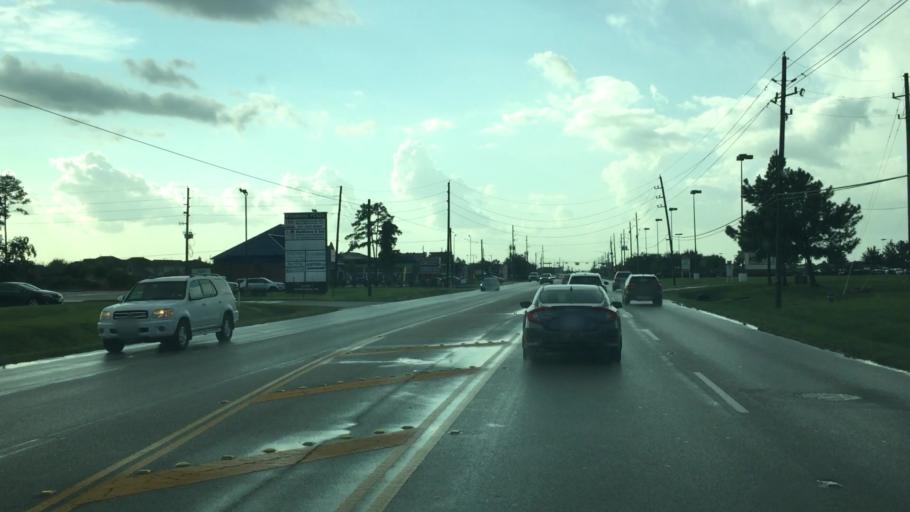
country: US
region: Texas
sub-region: Harris County
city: Spring
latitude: 30.0682
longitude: -95.5071
